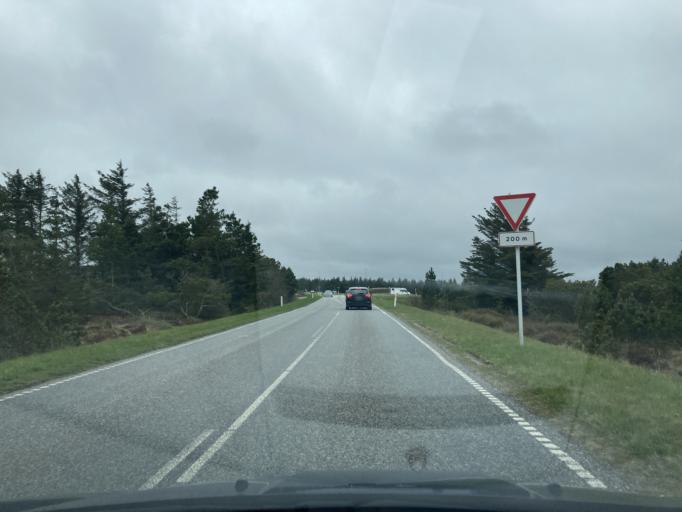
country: DK
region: North Denmark
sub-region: Thisted Kommune
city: Hurup
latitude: 56.9215
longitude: 8.3736
